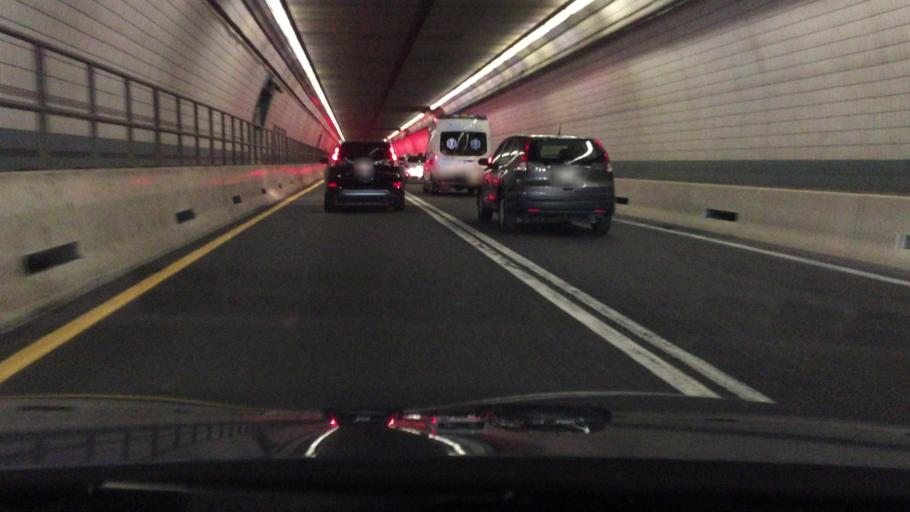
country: US
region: Massachusetts
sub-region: Suffolk County
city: Boston
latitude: 42.3575
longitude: -71.0325
